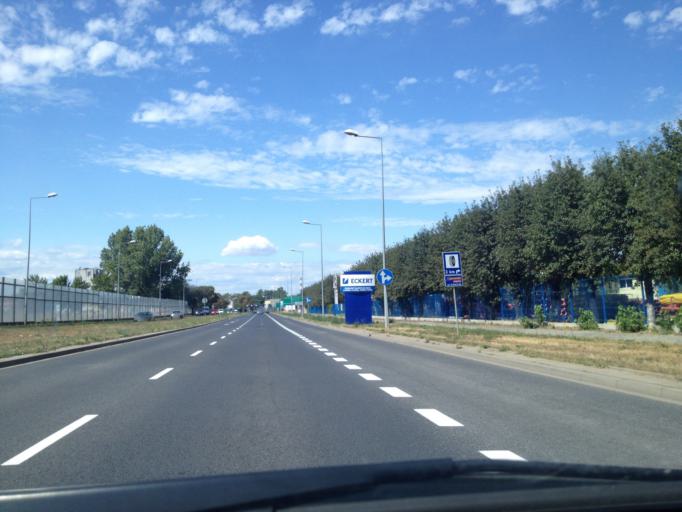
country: PL
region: Lower Silesian Voivodeship
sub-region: Legnica
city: Legnica
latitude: 51.1765
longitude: 16.1638
